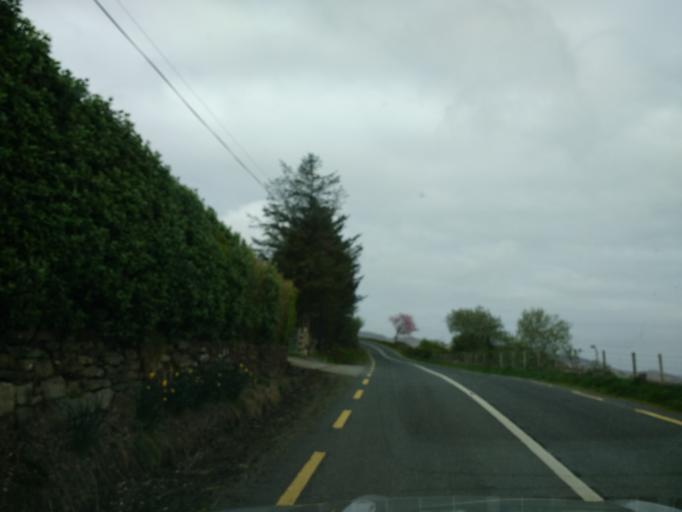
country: IE
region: Ulster
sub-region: County Donegal
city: Buncrana
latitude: 55.1542
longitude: -7.5555
